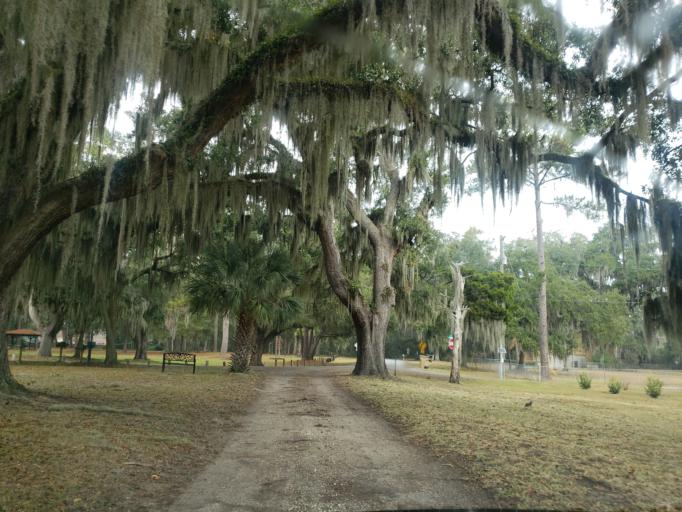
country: US
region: Georgia
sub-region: Chatham County
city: Wilmington Island
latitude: 31.9743
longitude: -80.9977
